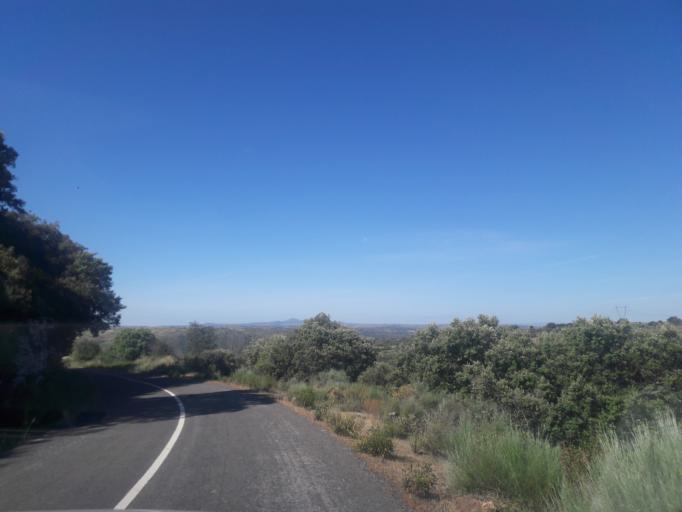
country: ES
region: Castille and Leon
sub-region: Provincia de Salamanca
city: Saucelle
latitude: 41.0345
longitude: -6.7699
